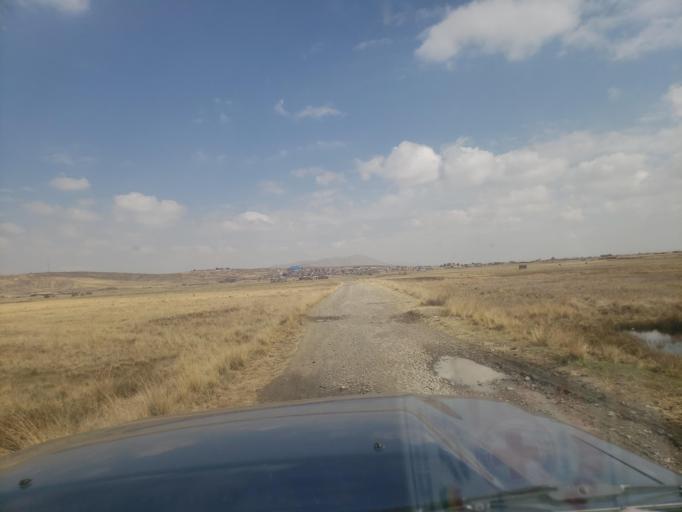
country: BO
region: La Paz
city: Batallas
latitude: -16.4046
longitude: -68.4591
